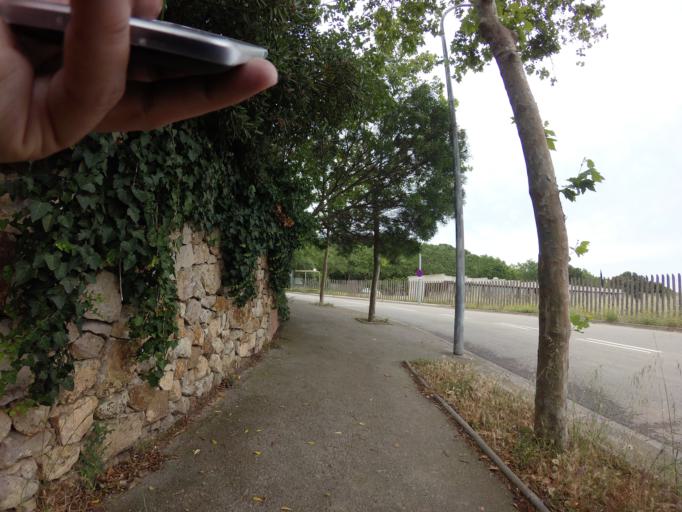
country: ES
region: Catalonia
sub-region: Provincia de Barcelona
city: Sants-Montjuic
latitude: 41.3630
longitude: 2.1610
